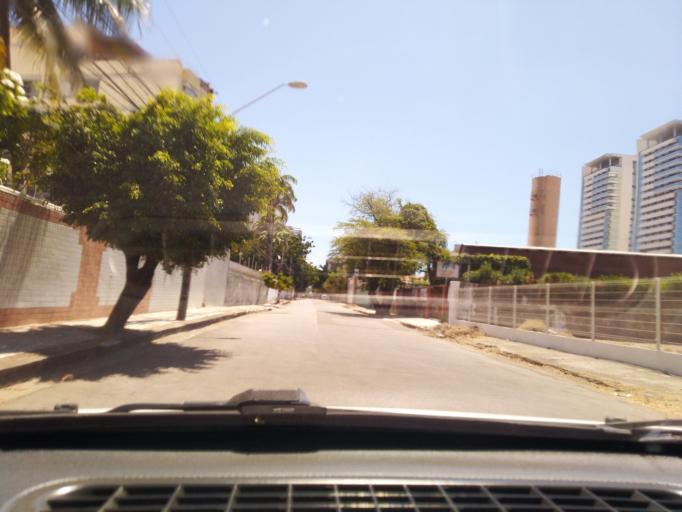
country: BR
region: Ceara
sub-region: Fortaleza
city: Fortaleza
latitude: -3.7436
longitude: -38.4785
